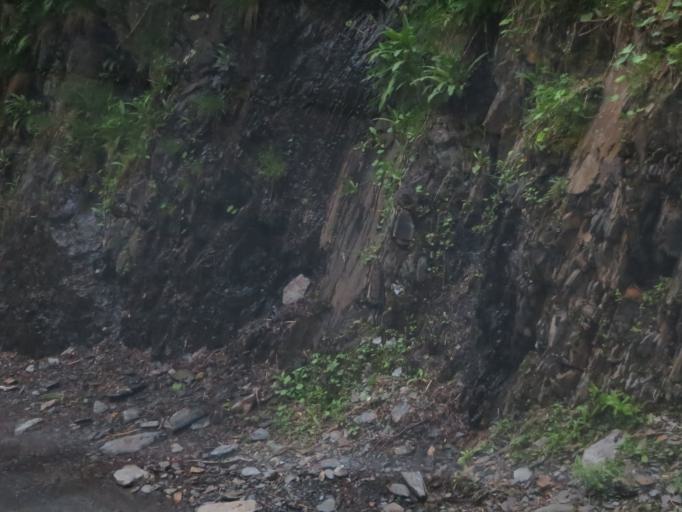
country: GE
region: Kakheti
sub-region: Telavi
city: Telavi
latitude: 42.2322
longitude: 45.4869
